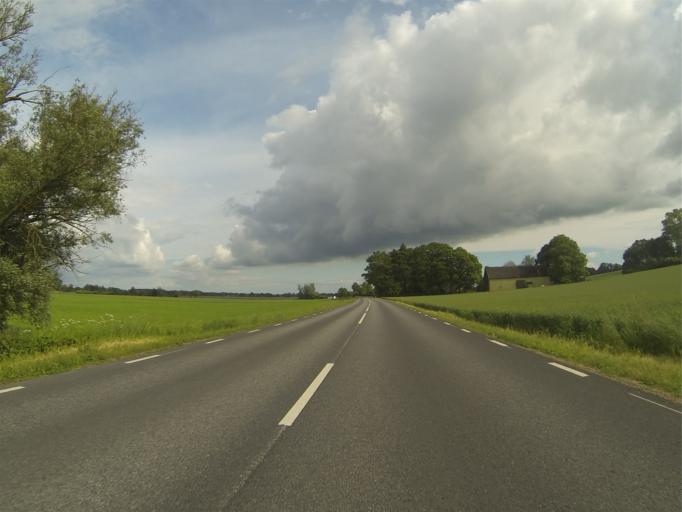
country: SE
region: Skane
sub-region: Eslovs Kommun
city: Eslov
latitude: 55.7558
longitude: 13.3194
